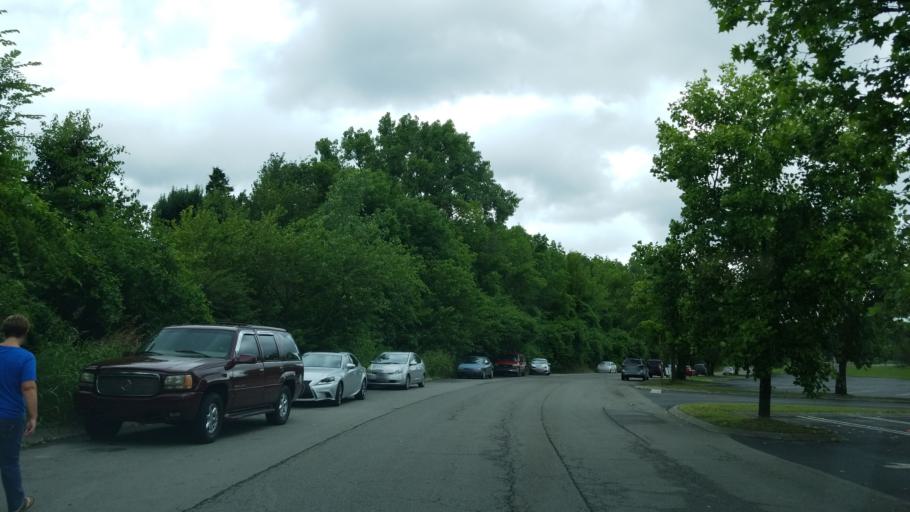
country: US
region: Tennessee
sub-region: Rutherford County
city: La Vergne
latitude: 36.0510
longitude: -86.6598
